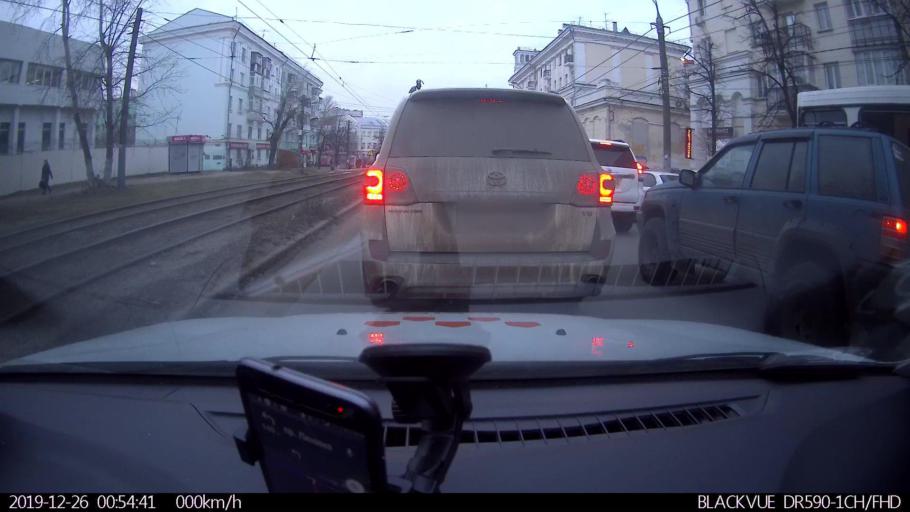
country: RU
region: Nizjnij Novgorod
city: Nizhniy Novgorod
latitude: 56.3007
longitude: 43.9416
